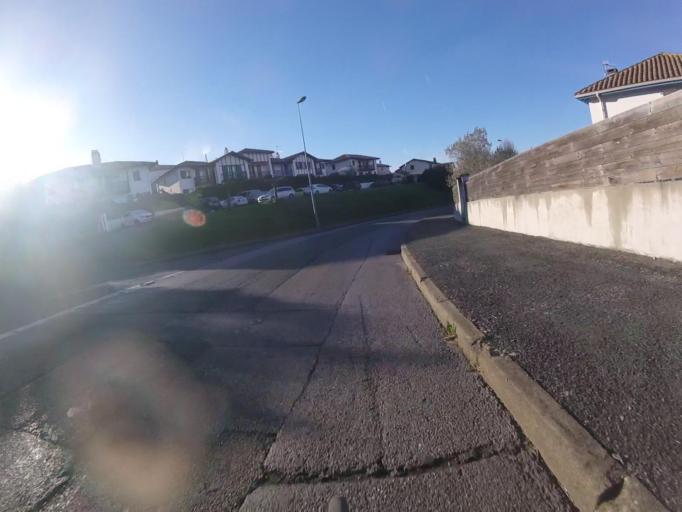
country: FR
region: Aquitaine
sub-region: Departement des Pyrenees-Atlantiques
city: Hendaye
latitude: 43.3594
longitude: -1.7633
